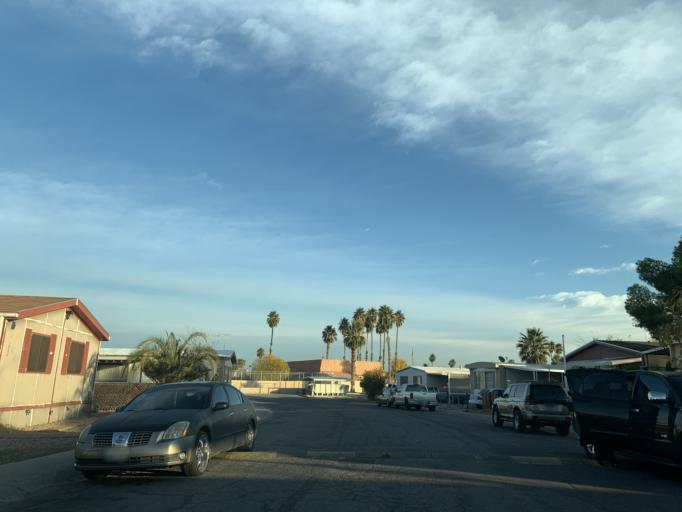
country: US
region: Nevada
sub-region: Clark County
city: Spring Valley
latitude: 36.1018
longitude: -115.2212
